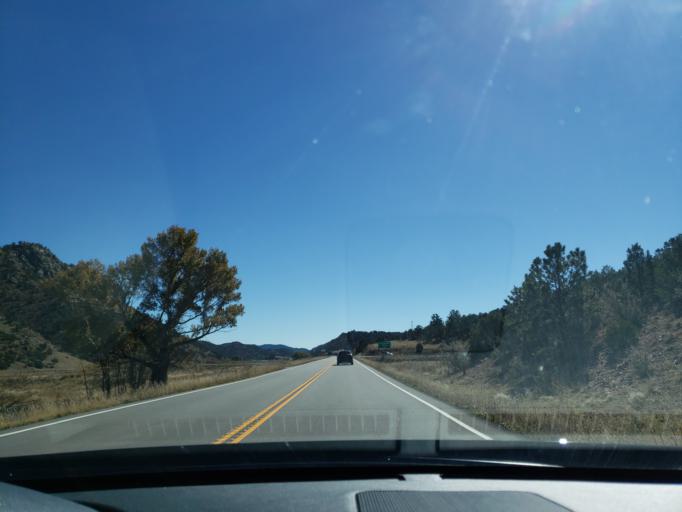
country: US
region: Colorado
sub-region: Fremont County
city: Canon City
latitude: 38.6134
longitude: -105.4430
